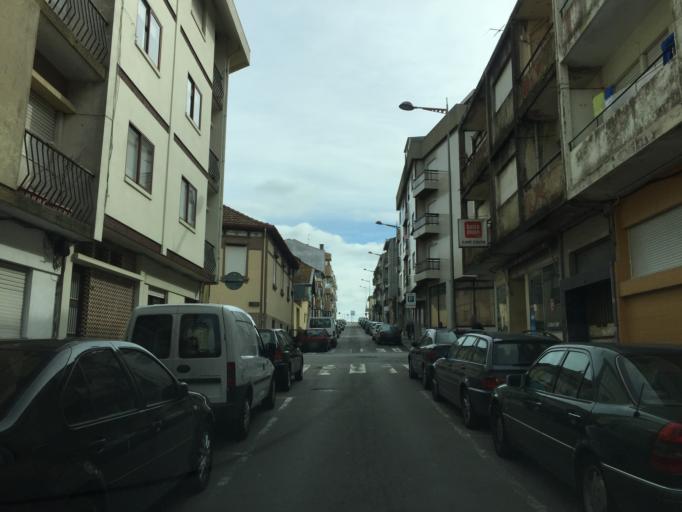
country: PT
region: Porto
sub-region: Vila Nova de Gaia
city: Vila Nova de Gaia
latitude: 41.1356
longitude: -8.6067
